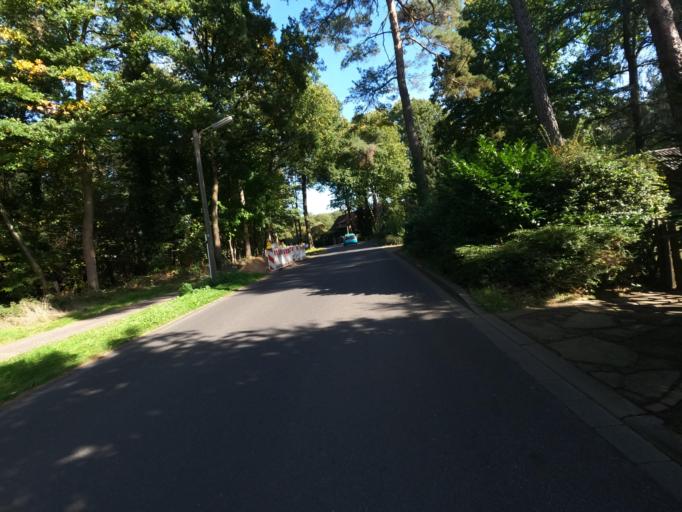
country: DE
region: North Rhine-Westphalia
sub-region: Regierungsbezirk Koln
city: Wassenberg
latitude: 51.0965
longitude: 6.1710
